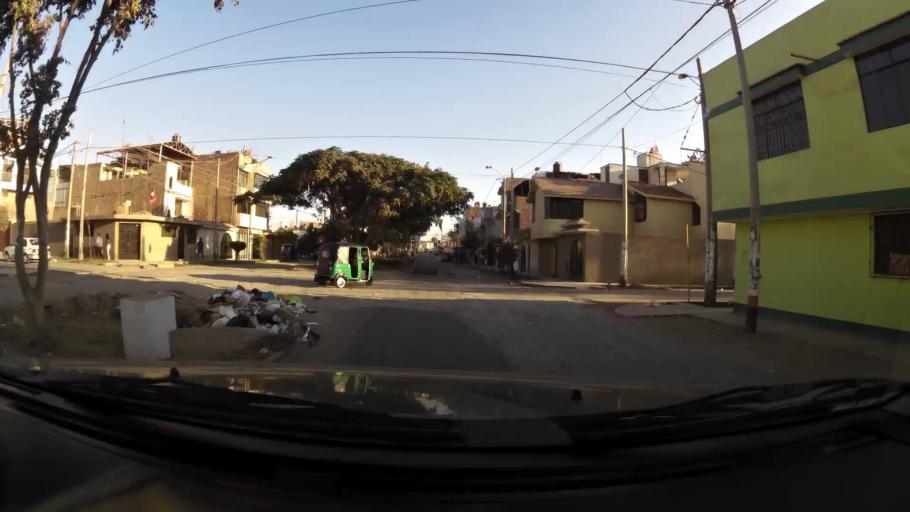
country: PE
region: Ica
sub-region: Provincia de Ica
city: Ica
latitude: -14.0586
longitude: -75.7343
